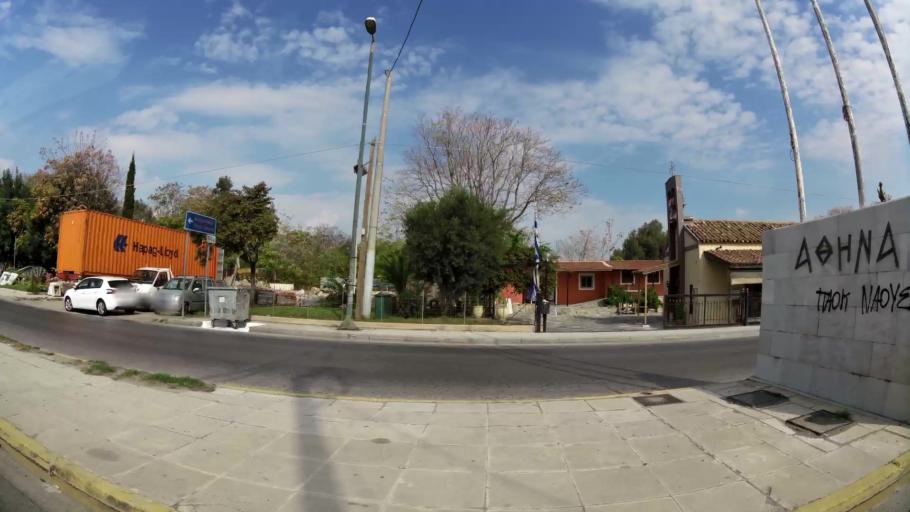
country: GR
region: Attica
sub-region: Nomarchia Athinas
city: Aigaleo
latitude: 37.9871
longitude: 23.6958
